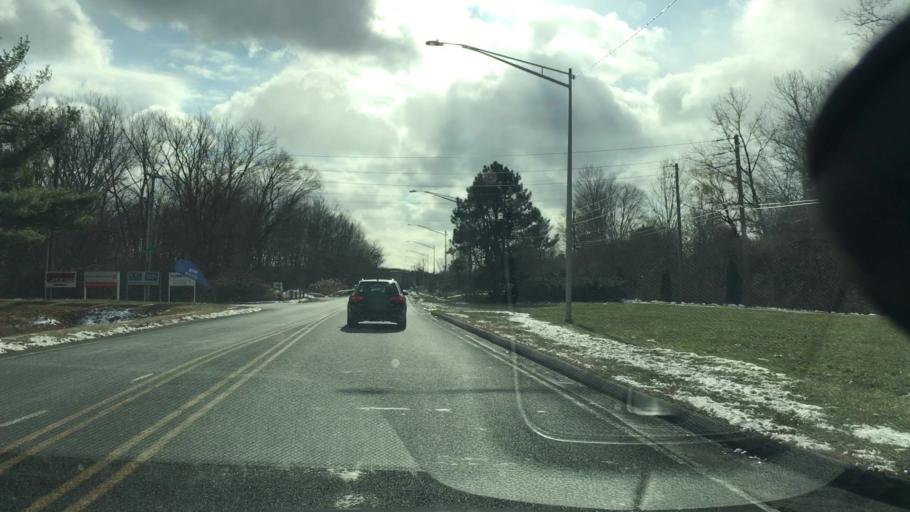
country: US
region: Connecticut
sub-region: New Haven County
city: Meriden
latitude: 41.5117
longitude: -72.7673
